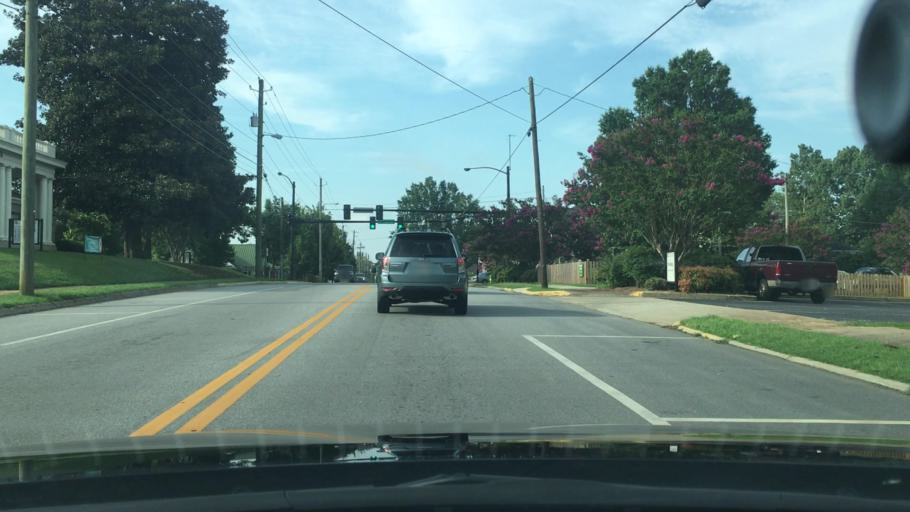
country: US
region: Georgia
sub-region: Spalding County
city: Griffin
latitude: 33.2465
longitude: -84.2656
